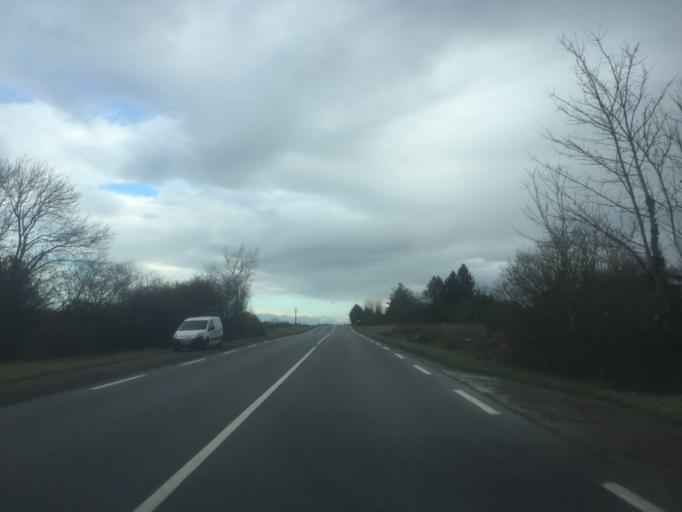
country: FR
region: Franche-Comte
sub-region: Departement du Jura
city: Fraisans
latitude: 47.1684
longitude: 5.7739
